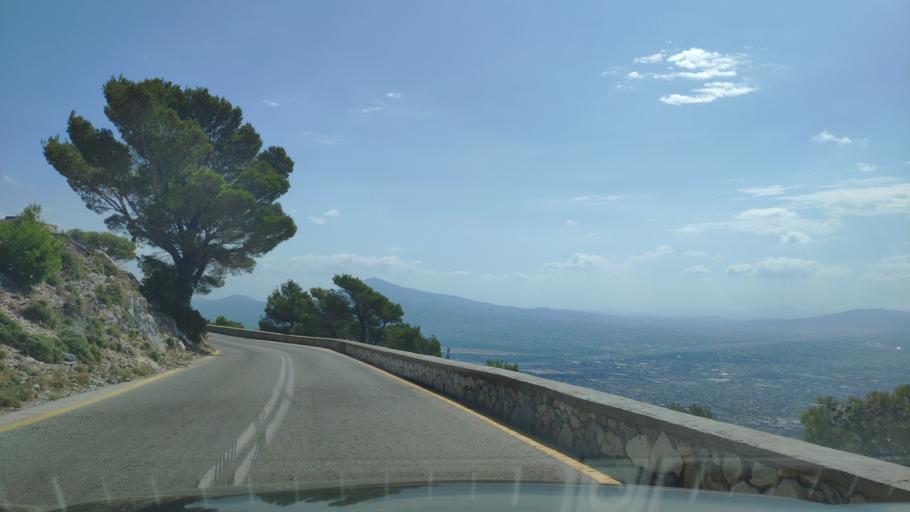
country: GR
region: Attica
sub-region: Nomarchia Anatolikis Attikis
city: Thrakomakedones
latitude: 38.1406
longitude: 23.7146
